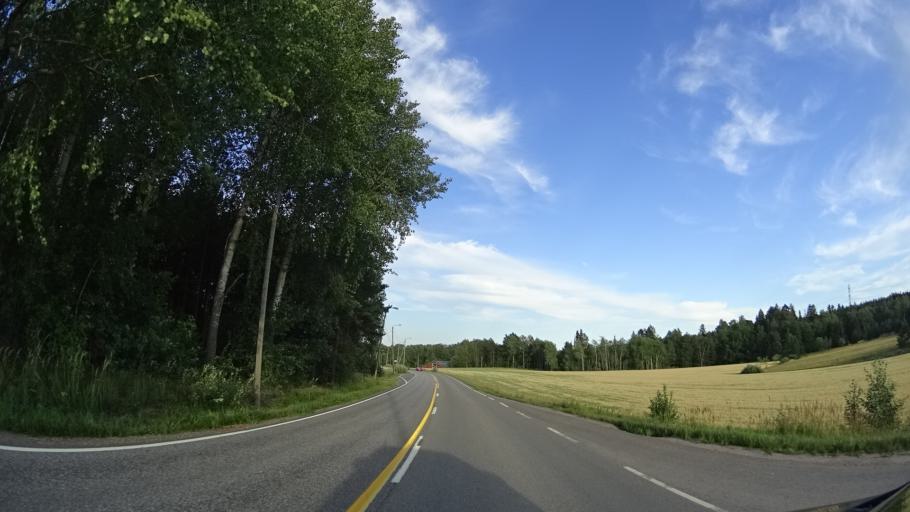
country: FI
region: Uusimaa
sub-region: Helsinki
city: Kirkkonummi
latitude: 60.2059
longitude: 24.4944
